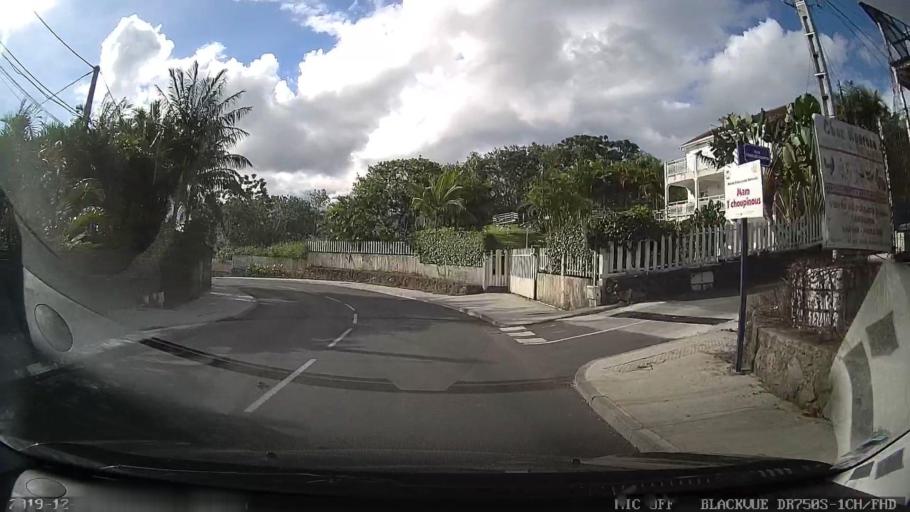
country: RE
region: Reunion
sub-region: Reunion
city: Le Tampon
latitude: -21.2462
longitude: 55.5169
